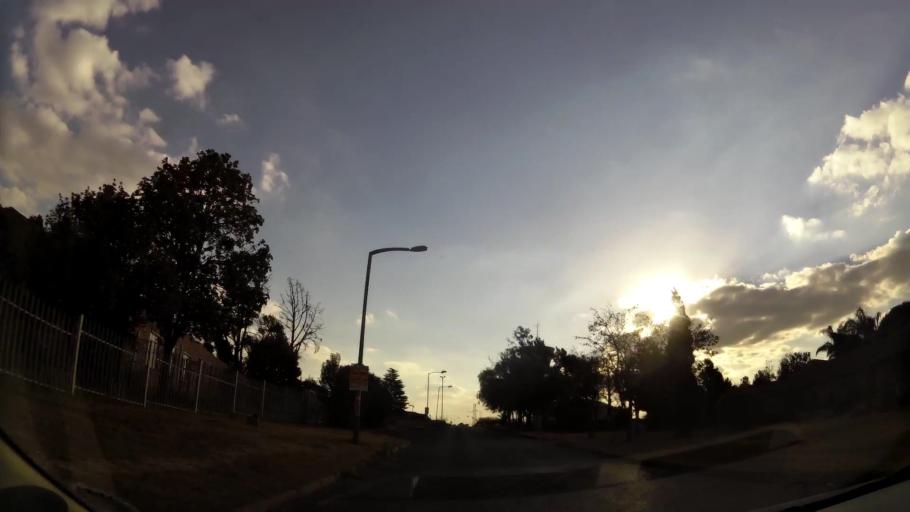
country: ZA
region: Gauteng
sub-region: West Rand District Municipality
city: Krugersdorp
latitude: -26.0725
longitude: 27.7641
